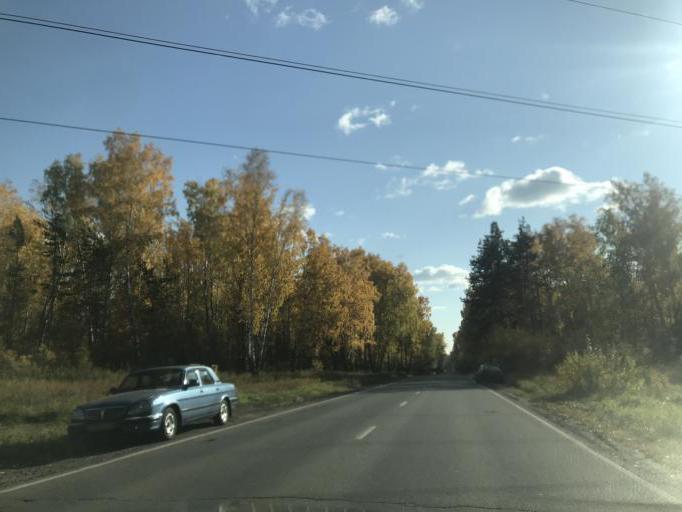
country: RU
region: Chelyabinsk
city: Dolgoderevenskoye
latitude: 55.2700
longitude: 61.3650
